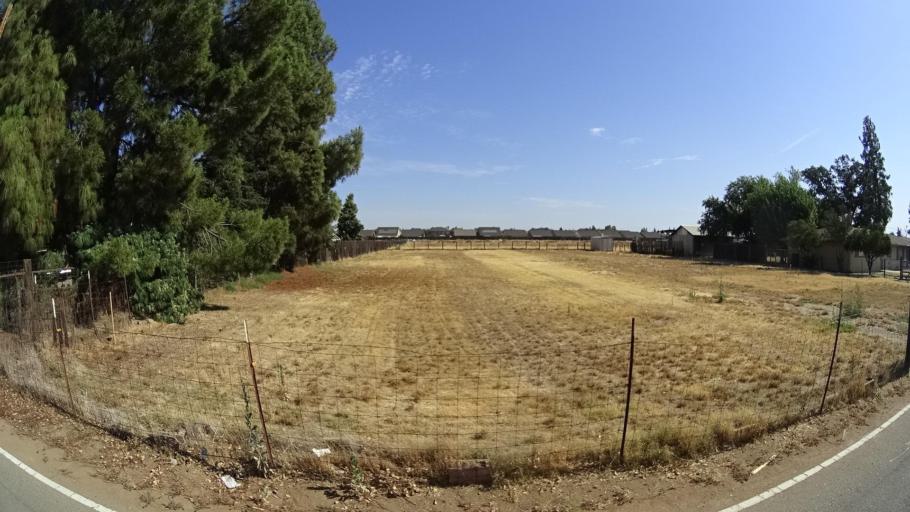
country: US
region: California
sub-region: Fresno County
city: Tarpey Village
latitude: 36.7866
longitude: -119.6749
